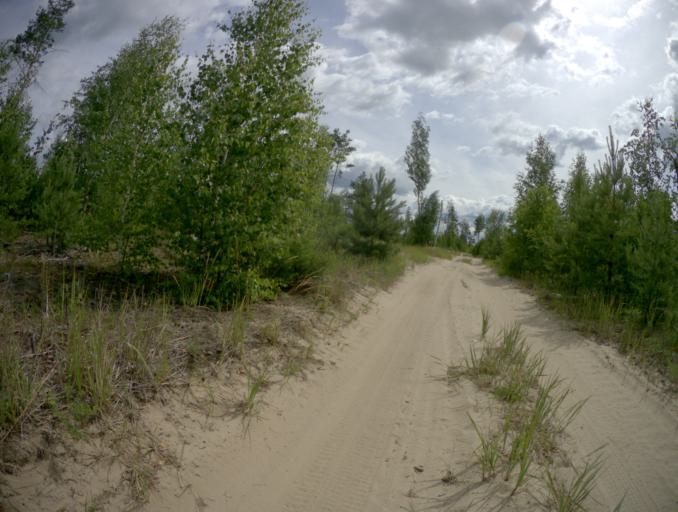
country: RU
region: Nizjnij Novgorod
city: Frolishchi
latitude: 56.5061
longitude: 42.5261
